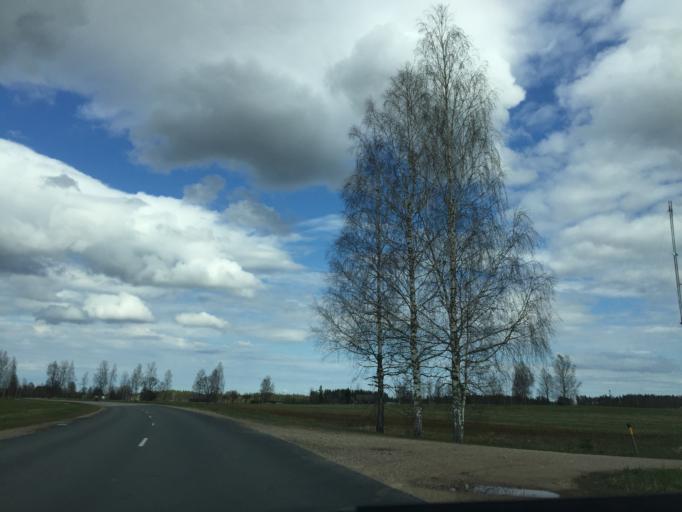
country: LV
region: Gulbenes Rajons
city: Gulbene
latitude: 57.2541
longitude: 26.5478
